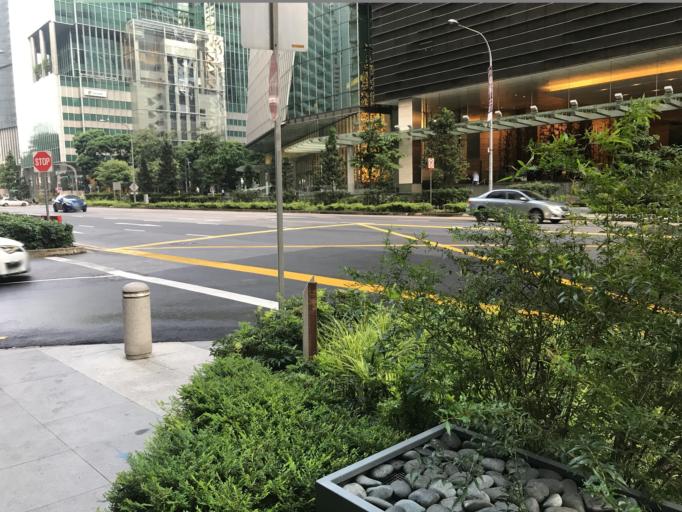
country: SG
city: Singapore
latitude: 1.2808
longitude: 103.8512
